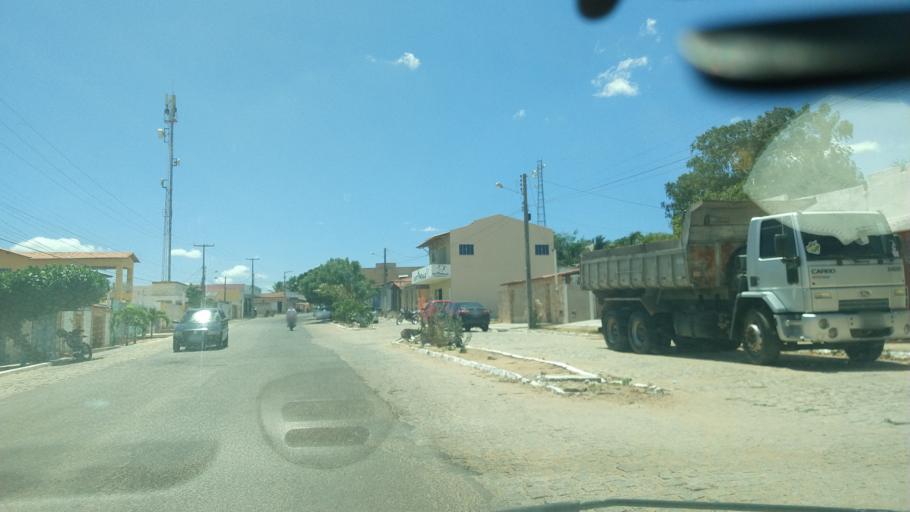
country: BR
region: Rio Grande do Norte
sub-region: Cerro Cora
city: Cerro Cora
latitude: -6.0514
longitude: -36.3537
